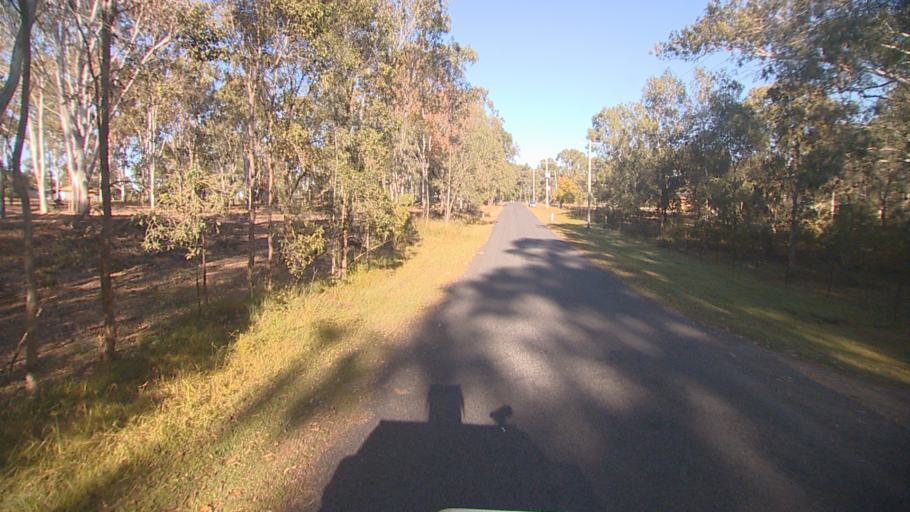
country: AU
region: Queensland
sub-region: Logan
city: North Maclean
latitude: -27.7964
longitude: 152.9943
